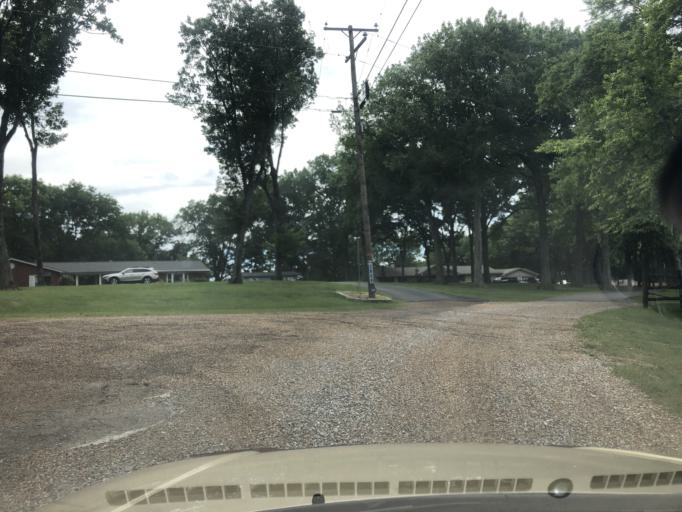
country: US
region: Tennessee
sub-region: Davidson County
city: Lakewood
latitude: 36.2239
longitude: -86.6469
